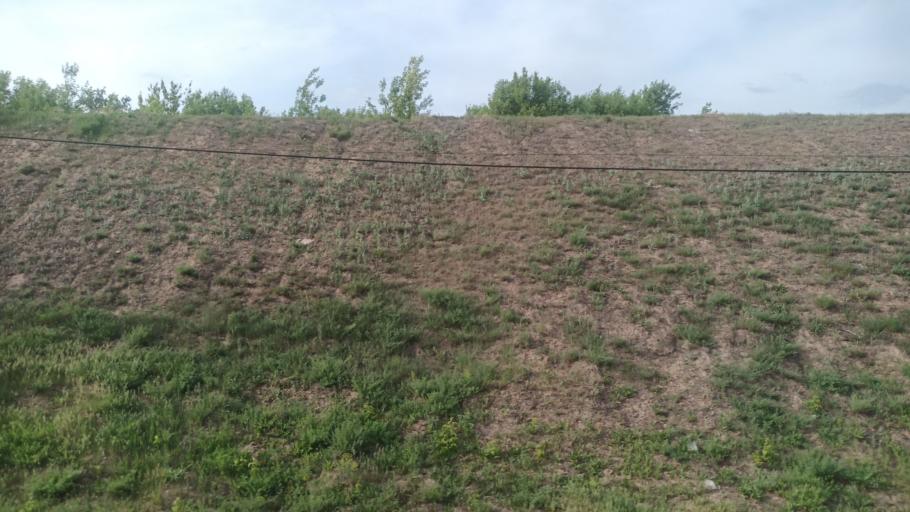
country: RU
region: Altai Krai
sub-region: Gorod Barnaulskiy
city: Barnaul
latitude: 53.3729
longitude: 83.7889
